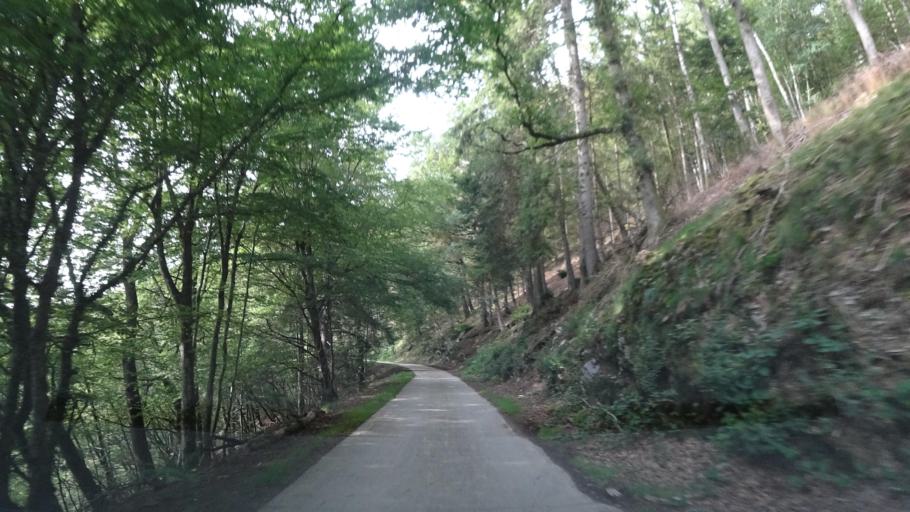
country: BE
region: Wallonia
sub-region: Province du Luxembourg
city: Herbeumont
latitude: 49.7711
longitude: 5.2492
